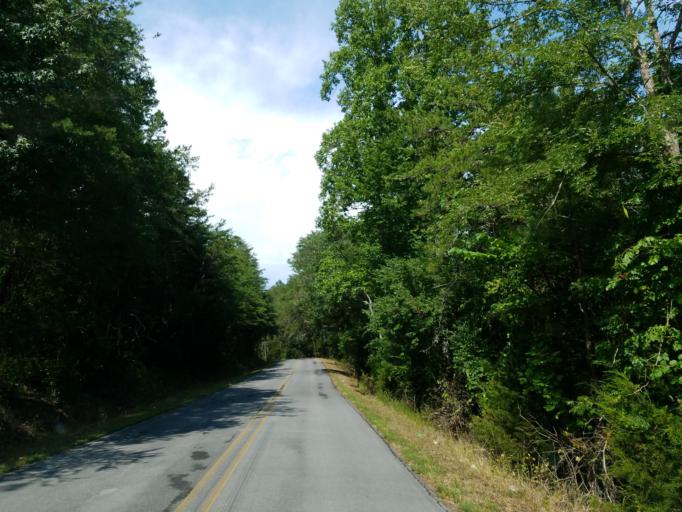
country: US
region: Georgia
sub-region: Bartow County
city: Rydal
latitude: 34.5364
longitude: -84.7227
